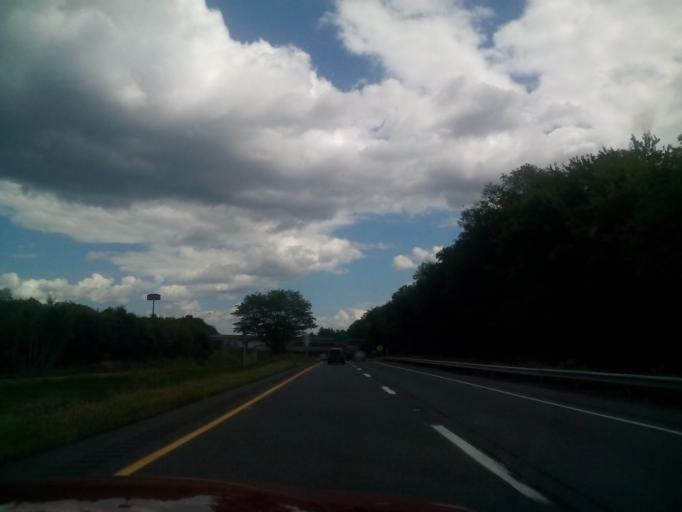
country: US
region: Pennsylvania
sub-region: Monroe County
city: Tannersville
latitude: 40.9991
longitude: -75.2727
